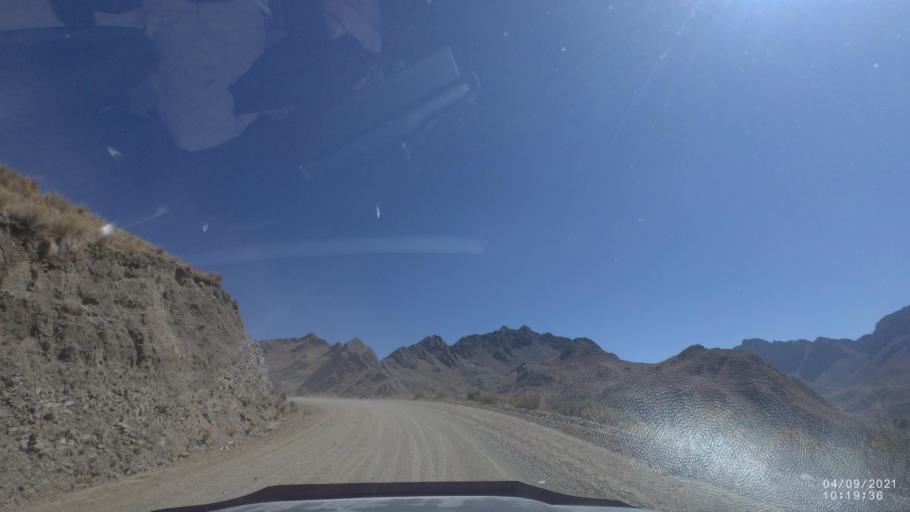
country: BO
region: Cochabamba
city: Sipe Sipe
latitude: -17.3164
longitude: -66.4258
